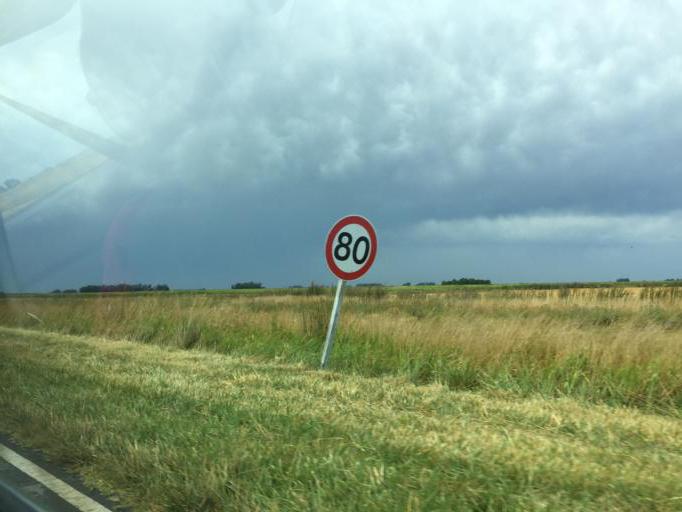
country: AR
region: Buenos Aires
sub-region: Partido de Rauch
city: Rauch
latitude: -37.0436
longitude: -59.0007
